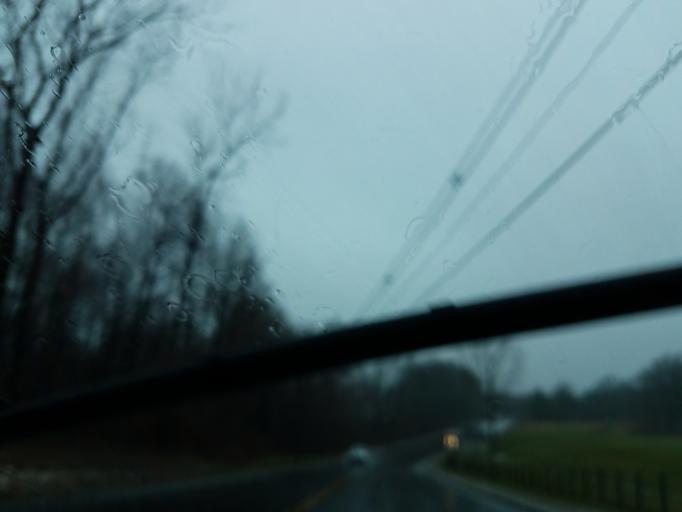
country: US
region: Connecticut
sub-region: New Haven County
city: Waterbury
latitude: 41.5319
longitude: -73.0668
